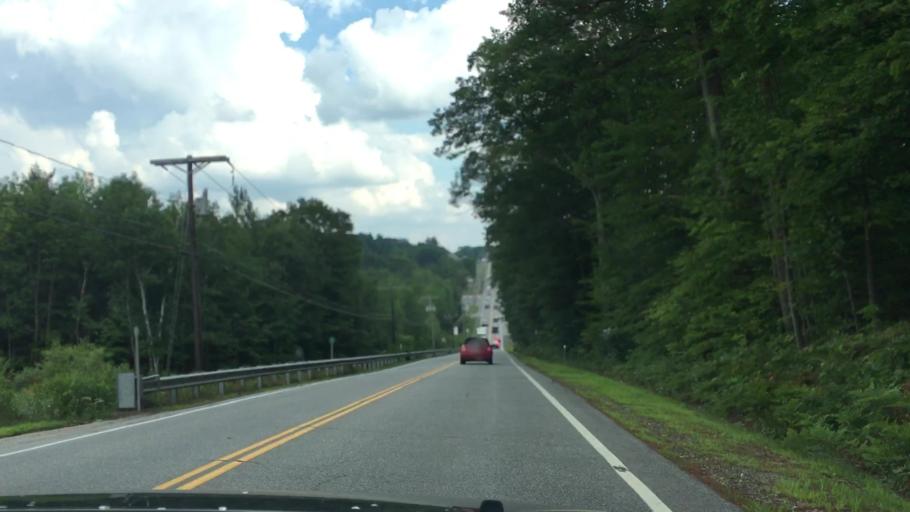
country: US
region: New Hampshire
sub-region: Belknap County
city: Meredith
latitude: 43.6210
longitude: -71.4840
